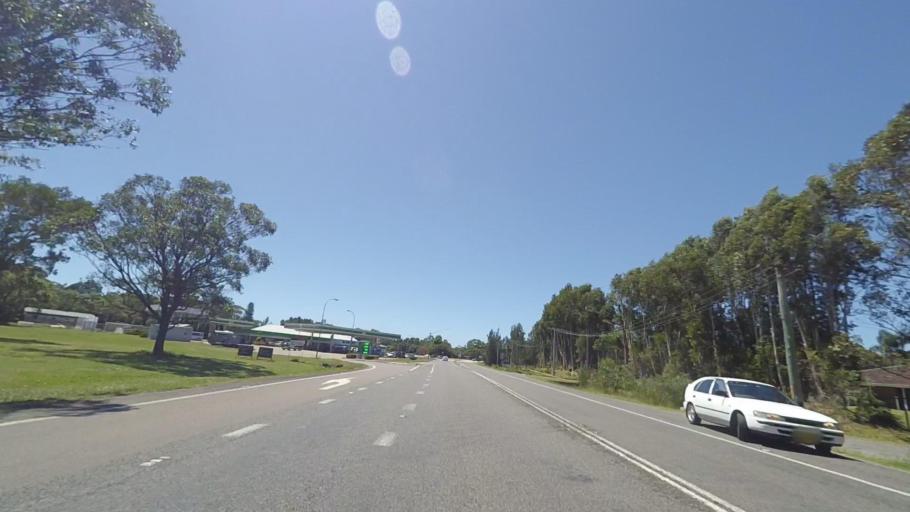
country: AU
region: New South Wales
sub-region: Port Stephens Shire
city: Medowie
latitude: -32.7881
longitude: 151.9011
